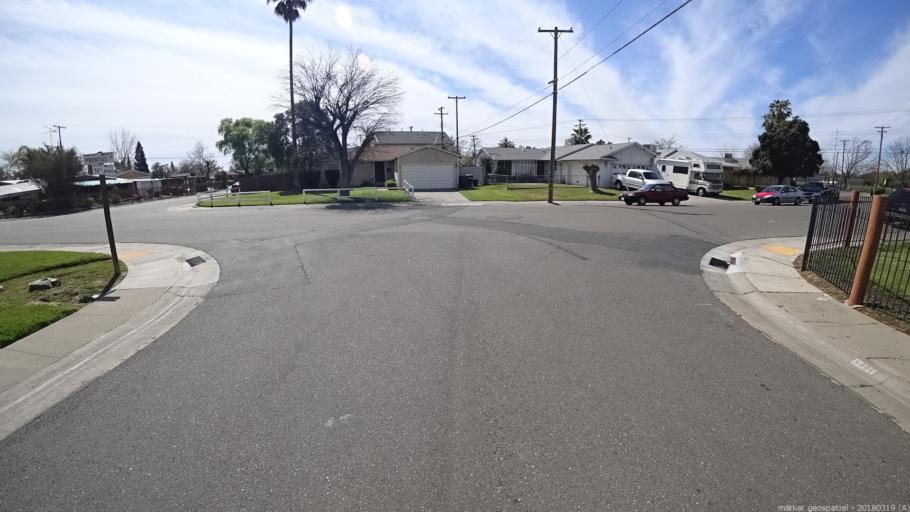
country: US
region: California
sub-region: Sacramento County
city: Parkway
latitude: 38.5079
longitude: -121.4409
